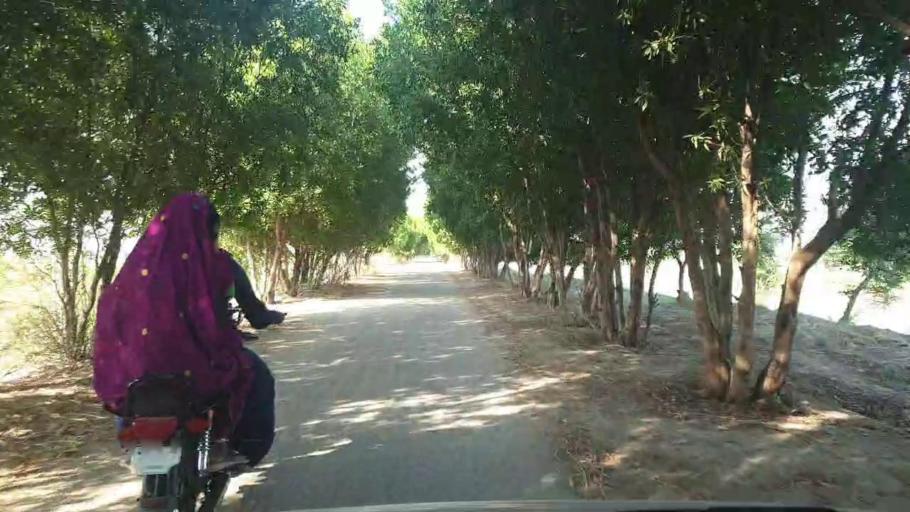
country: PK
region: Sindh
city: Badin
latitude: 24.6222
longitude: 68.8148
